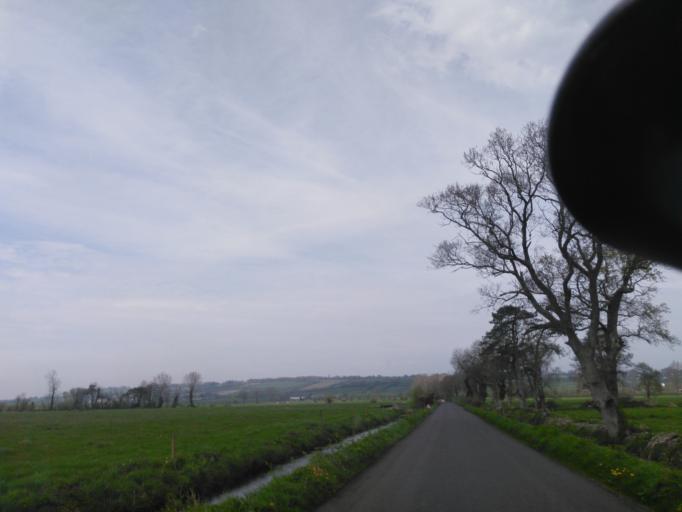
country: GB
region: England
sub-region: Somerset
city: Langport
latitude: 51.1141
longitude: -2.8226
